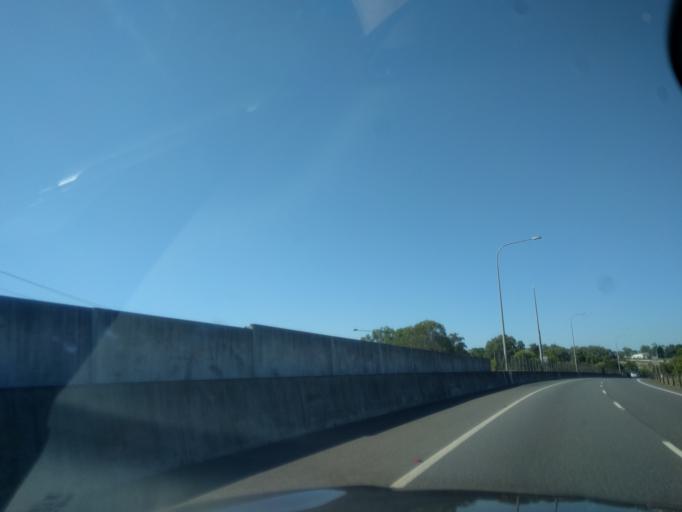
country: AU
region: Queensland
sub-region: Logan
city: Park Ridge South
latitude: -27.7148
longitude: 153.0338
